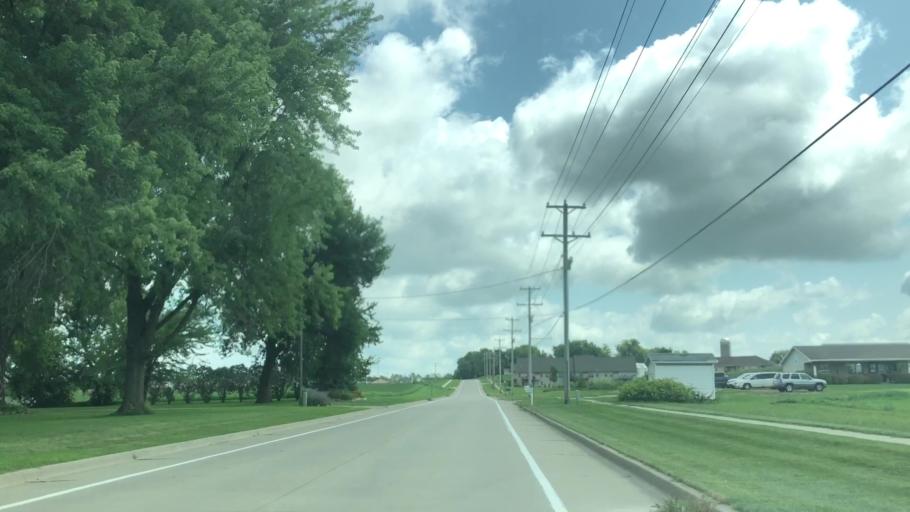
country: US
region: Iowa
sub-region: Marshall County
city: Marshalltown
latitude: 42.0178
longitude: -92.9517
